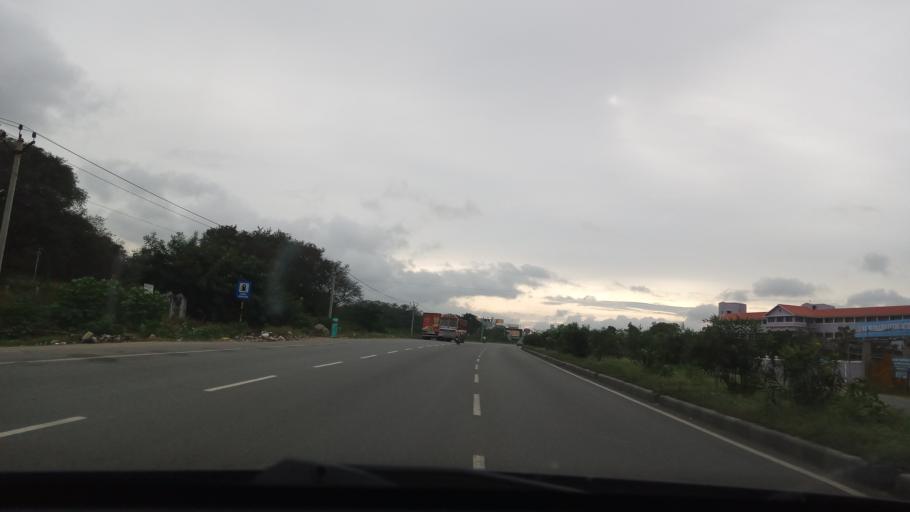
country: IN
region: Tamil Nadu
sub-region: Vellore
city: Vaniyambadi
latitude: 12.6571
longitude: 78.6058
